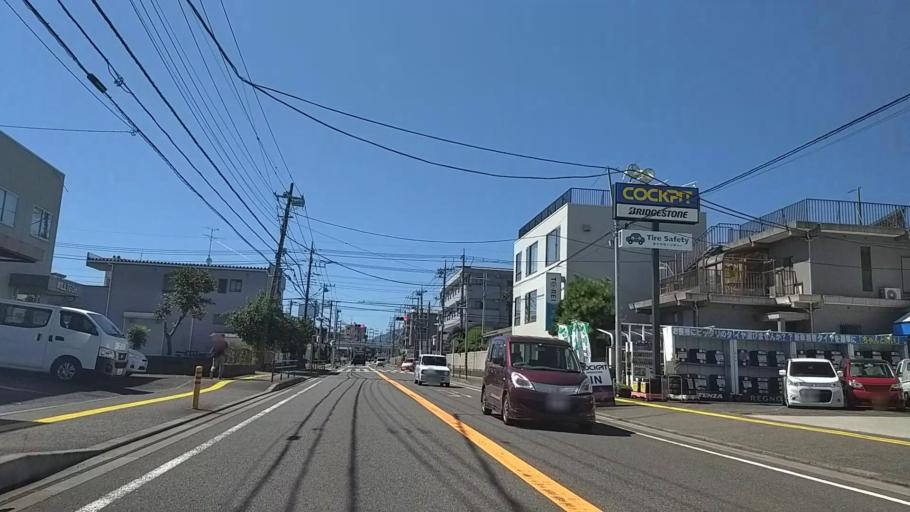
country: JP
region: Tokyo
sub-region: Machida-shi
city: Machida
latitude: 35.5718
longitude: 139.4037
